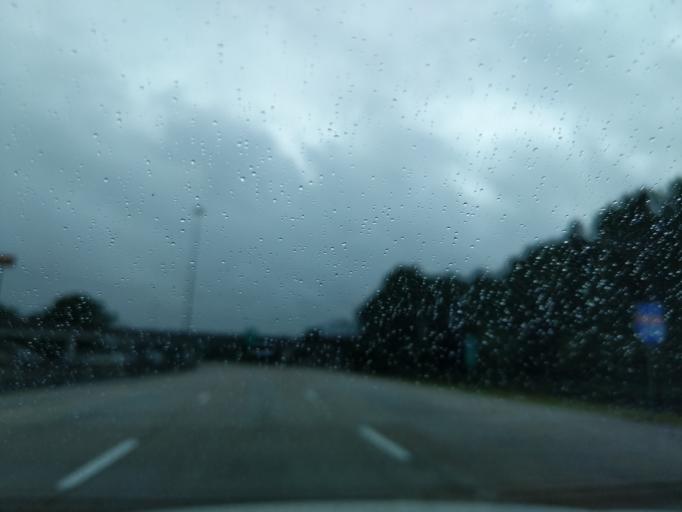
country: US
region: Mississippi
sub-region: Rankin County
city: Pearl
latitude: 32.2677
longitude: -90.1485
